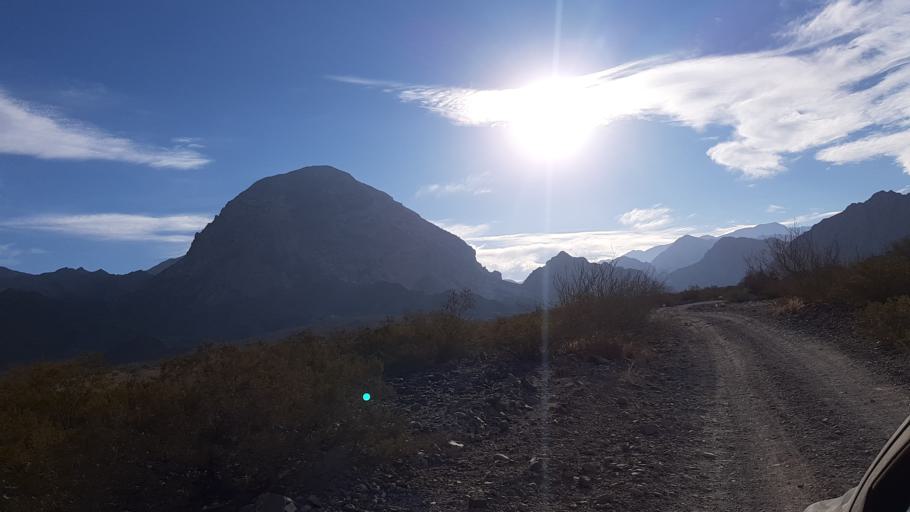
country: AR
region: San Juan
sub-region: Departamento de Zonda
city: Zonda
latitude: -31.4905
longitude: -68.8019
